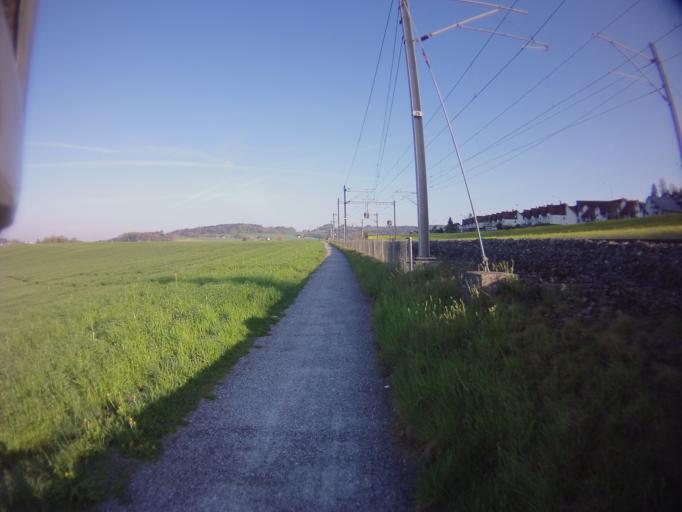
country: CH
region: Zurich
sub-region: Bezirk Affoltern
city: Affoltern / Unterdorf
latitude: 47.2895
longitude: 8.4502
